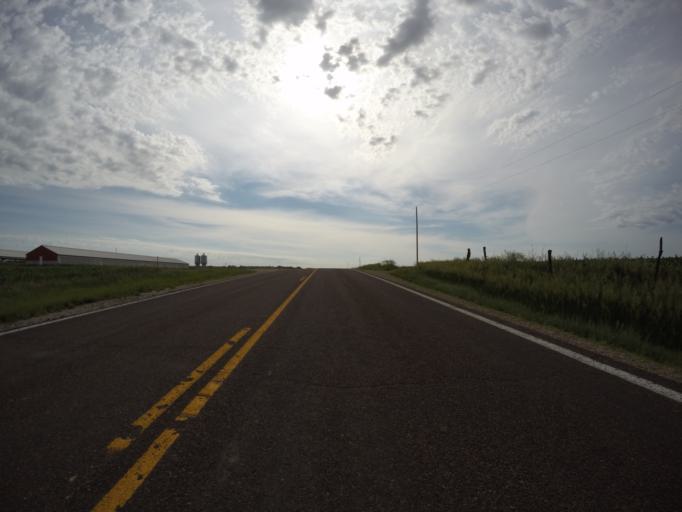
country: US
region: Kansas
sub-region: Washington County
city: Washington
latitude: 39.7121
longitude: -97.3338
